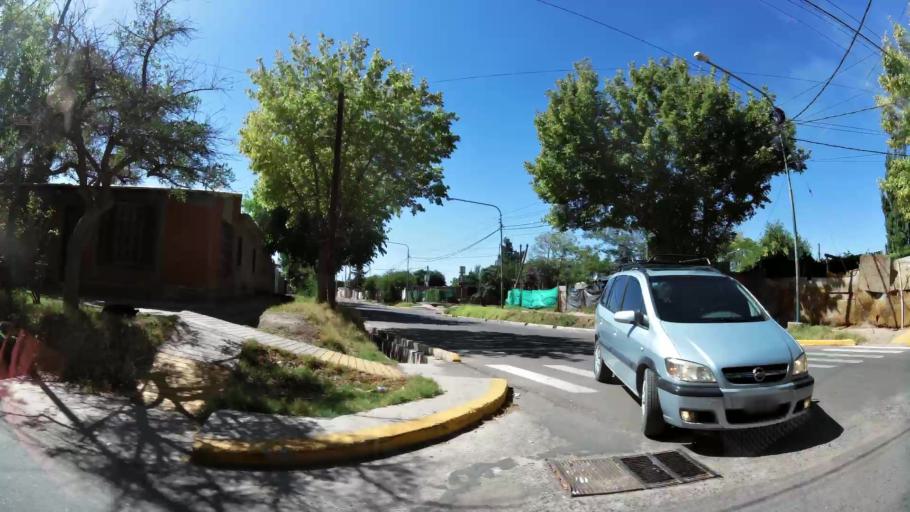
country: AR
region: Mendoza
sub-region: Departamento de Godoy Cruz
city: Godoy Cruz
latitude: -32.9579
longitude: -68.8417
